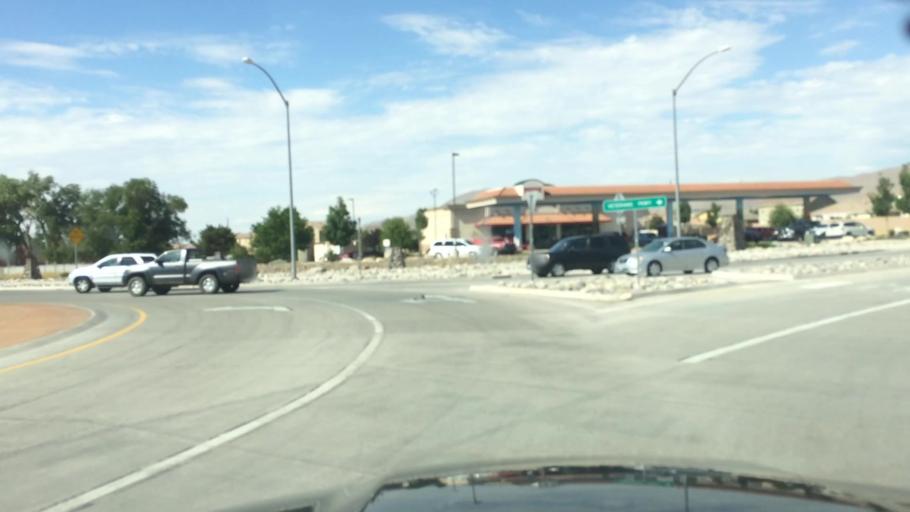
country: US
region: Nevada
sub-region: Storey County
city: Virginia City
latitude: 39.4025
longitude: -119.7415
